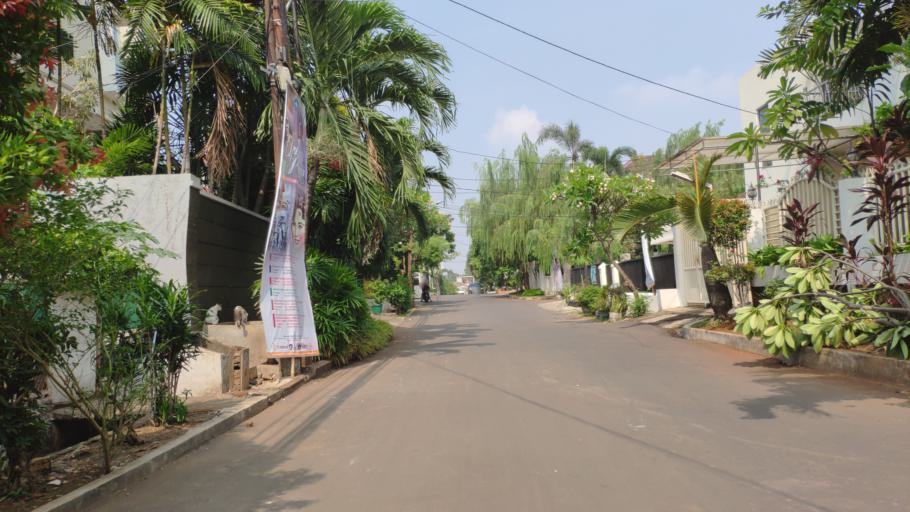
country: ID
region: Banten
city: South Tangerang
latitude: -6.2896
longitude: 106.7941
